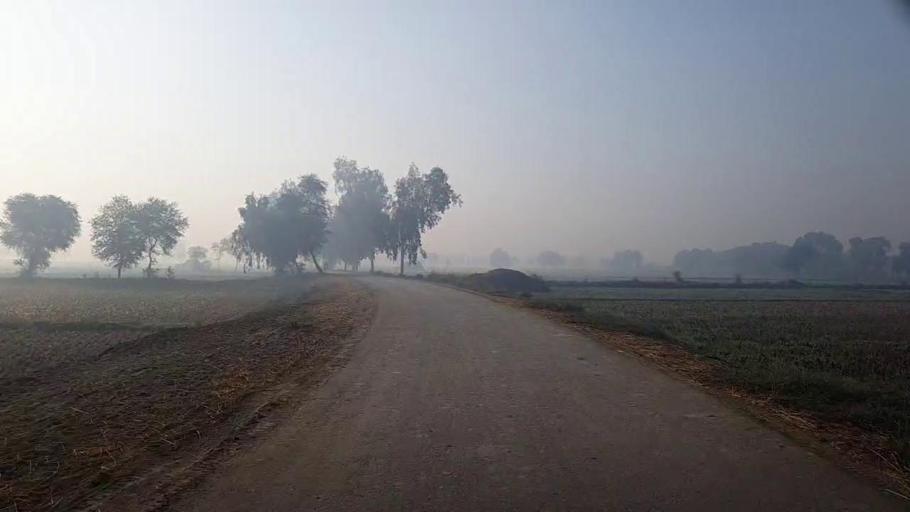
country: PK
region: Sindh
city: Mehar
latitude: 27.1439
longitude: 67.8227
